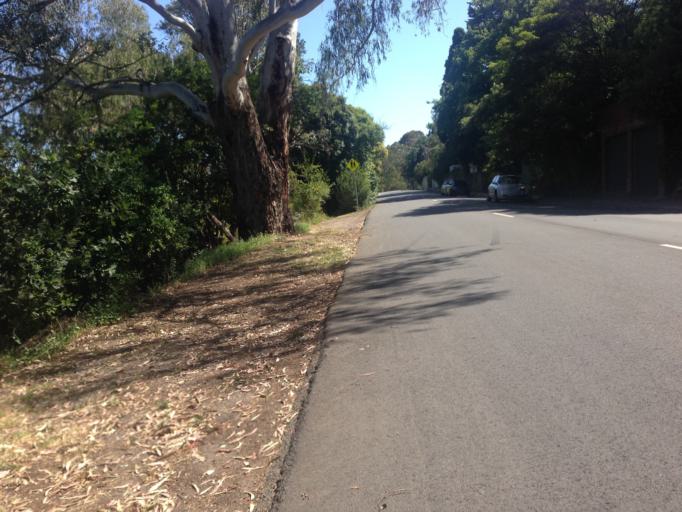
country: AU
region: Victoria
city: Ivanhoe East
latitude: -37.7770
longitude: 145.0457
